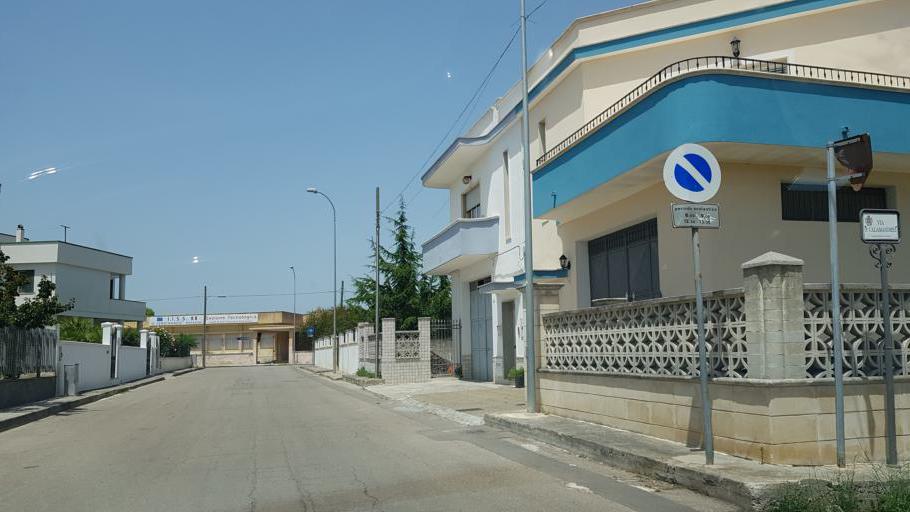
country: IT
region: Apulia
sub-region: Provincia di Brindisi
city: San Pancrazio Salentino
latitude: 40.4223
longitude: 17.8466
